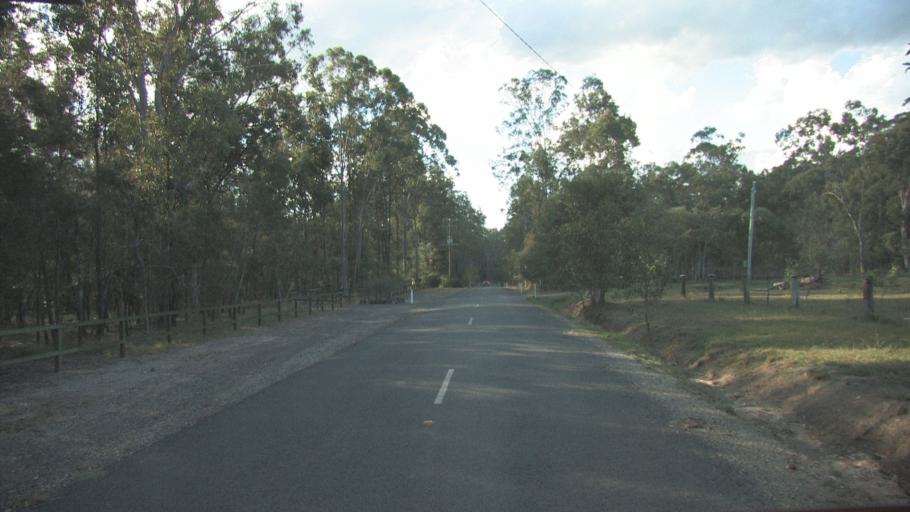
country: AU
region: Queensland
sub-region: Ipswich
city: Springfield Lakes
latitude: -27.6939
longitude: 152.9541
